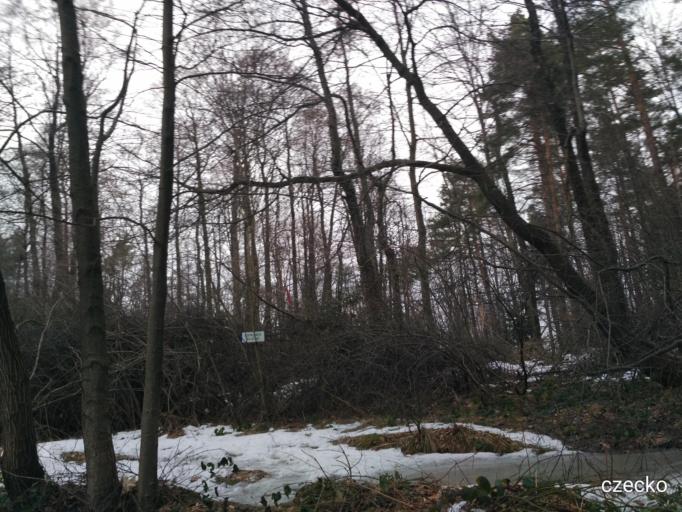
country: PL
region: Subcarpathian Voivodeship
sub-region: Powiat krosnienski
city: Korczyna
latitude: 49.7511
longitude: 21.8258
